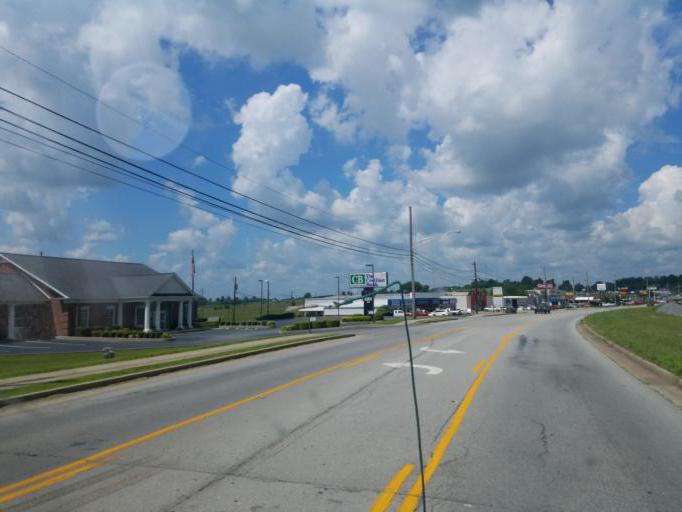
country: US
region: Kentucky
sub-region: Grayson County
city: Leitchfield
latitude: 37.4856
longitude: -86.2692
